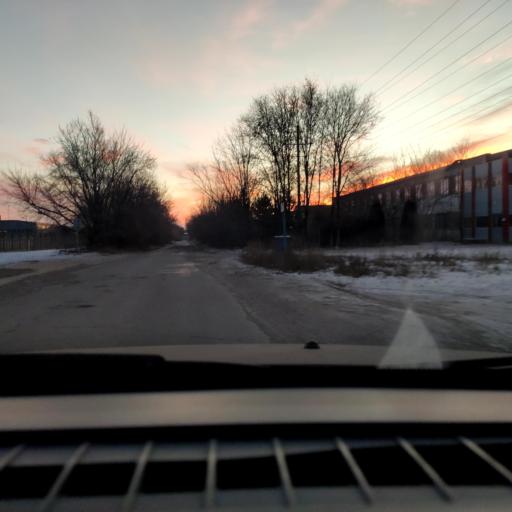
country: RU
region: Samara
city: Tol'yatti
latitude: 53.5787
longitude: 49.2700
